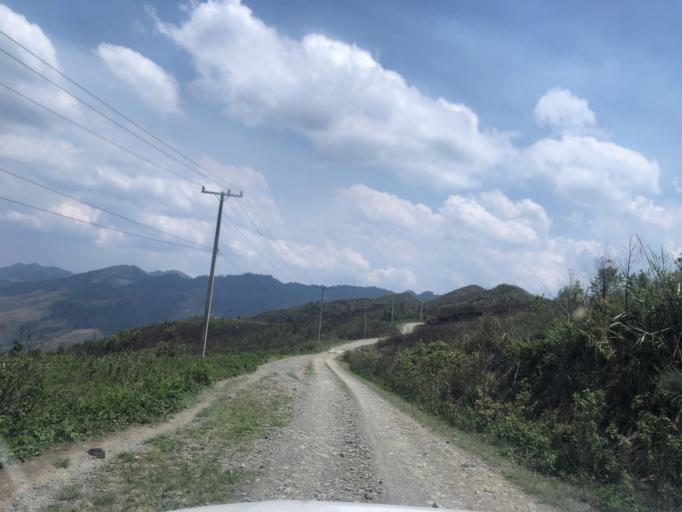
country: LA
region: Phongsali
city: Phongsali
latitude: 21.4181
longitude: 102.1844
